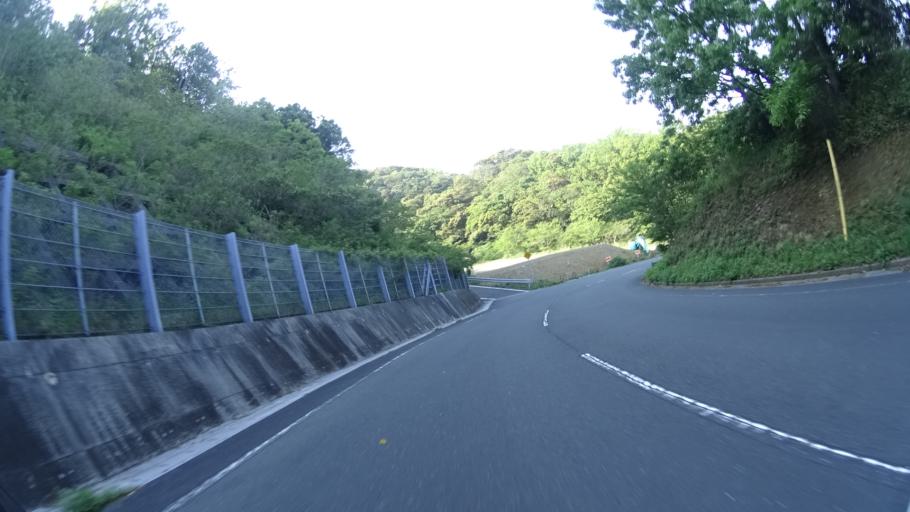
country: JP
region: Oita
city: Tsukumiura
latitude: 33.3597
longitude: 132.0394
